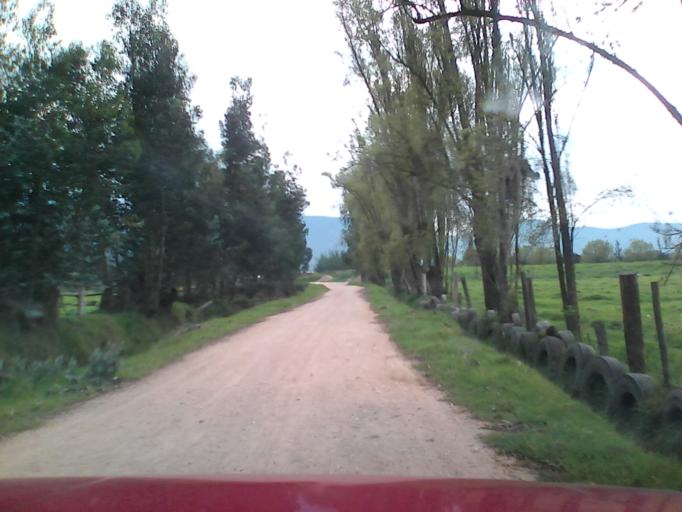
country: CO
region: Boyaca
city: Duitama
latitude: 5.8088
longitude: -73.0018
